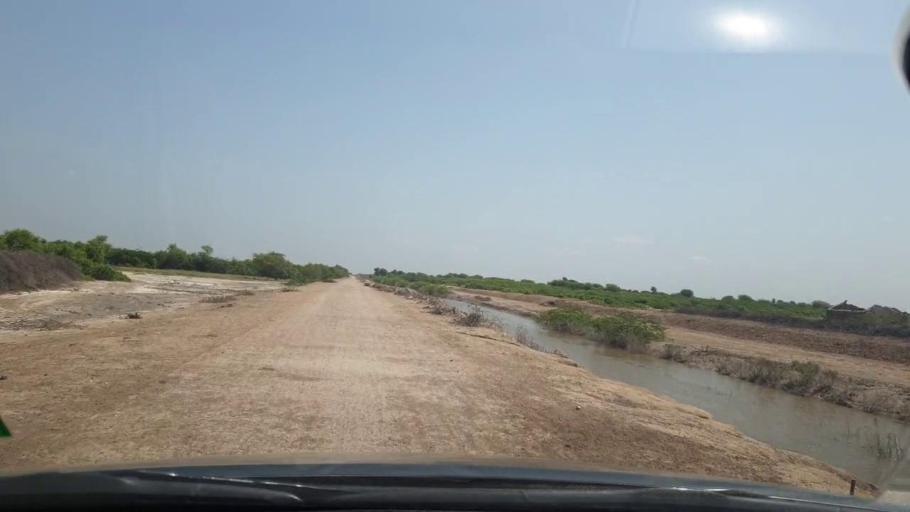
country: PK
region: Sindh
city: Tando Bago
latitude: 24.8927
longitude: 69.0992
